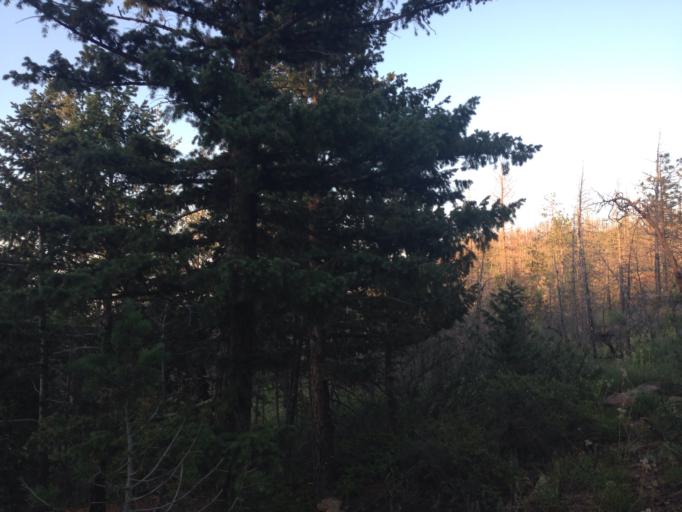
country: US
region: Colorado
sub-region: Larimer County
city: Laporte
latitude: 40.7120
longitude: -105.2936
